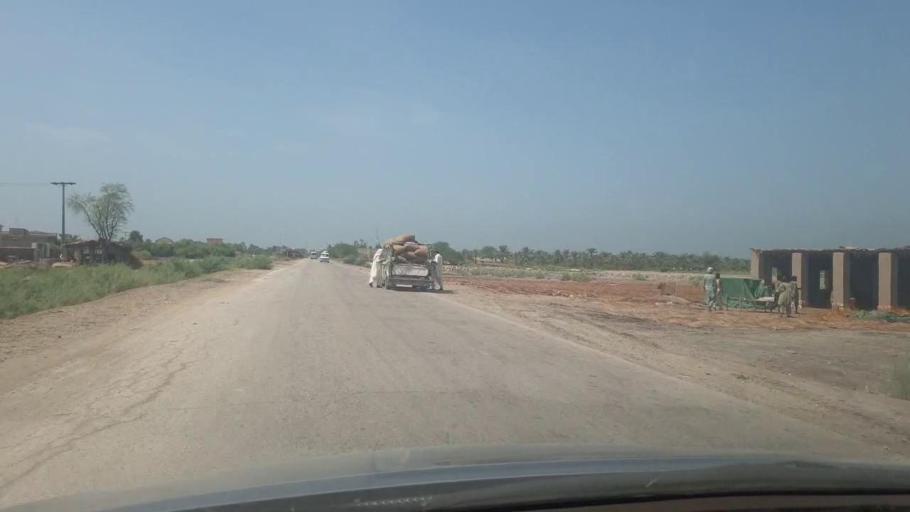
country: PK
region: Sindh
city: Ranipur
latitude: 27.2620
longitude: 68.5903
